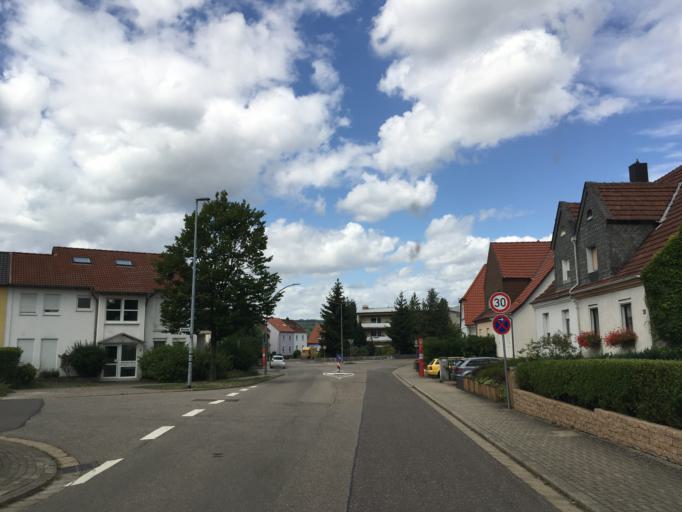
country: DE
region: Saarland
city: Sankt Ingbert
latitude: 49.2713
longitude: 7.1218
